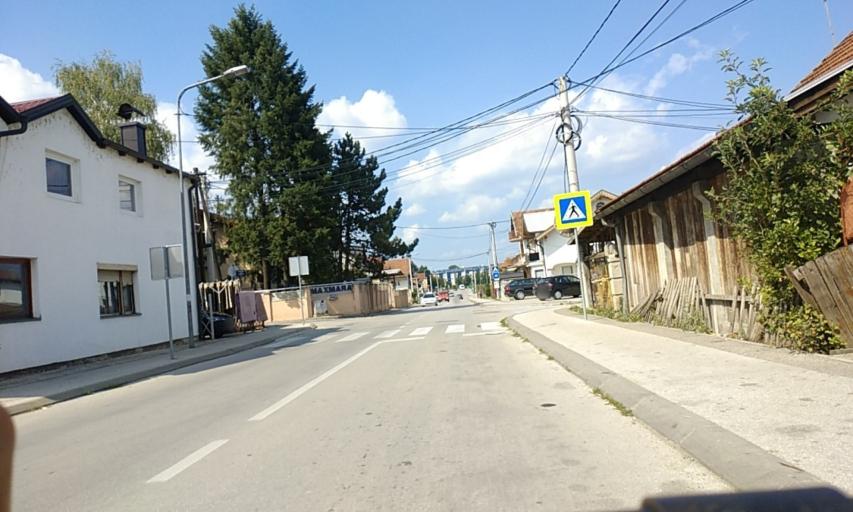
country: BA
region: Republika Srpska
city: Banja Luka
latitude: 44.7891
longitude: 17.1943
